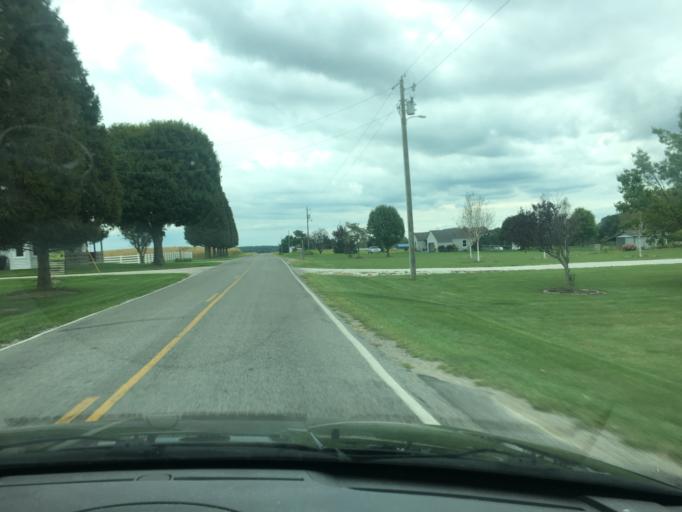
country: US
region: Ohio
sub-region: Logan County
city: West Liberty
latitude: 40.1923
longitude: -83.7584
